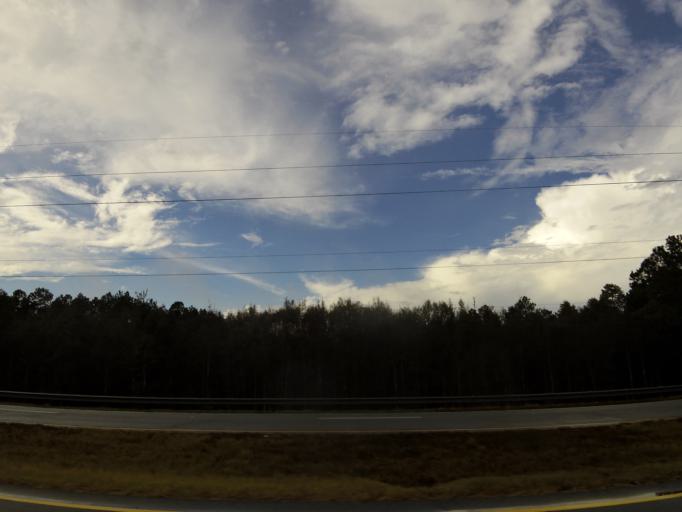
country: US
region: Georgia
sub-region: Long County
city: Ludowici
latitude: 31.6953
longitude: -81.7793
